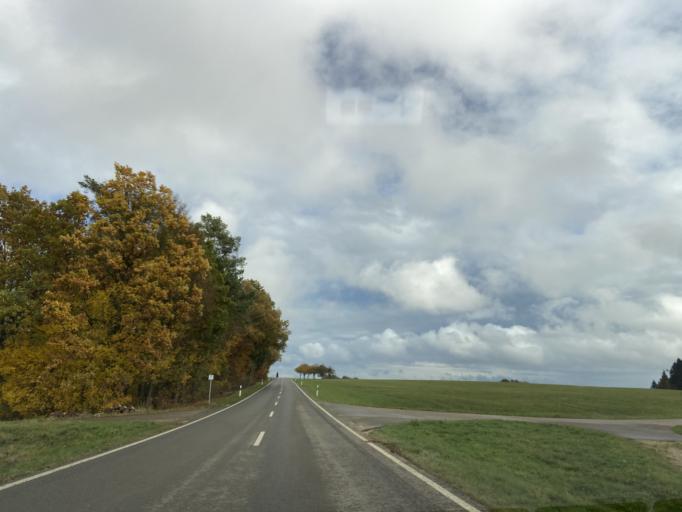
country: DE
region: Baden-Wuerttemberg
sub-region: Tuebingen Region
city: Messkirch
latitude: 48.0454
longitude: 9.1120
